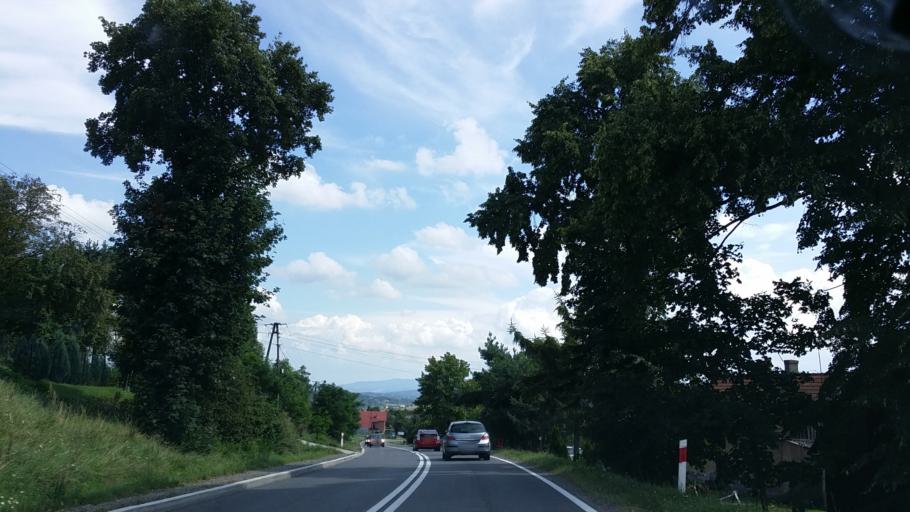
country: PL
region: Lesser Poland Voivodeship
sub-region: Powiat wielicki
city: Pawlikowice
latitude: 49.9261
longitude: 20.0732
